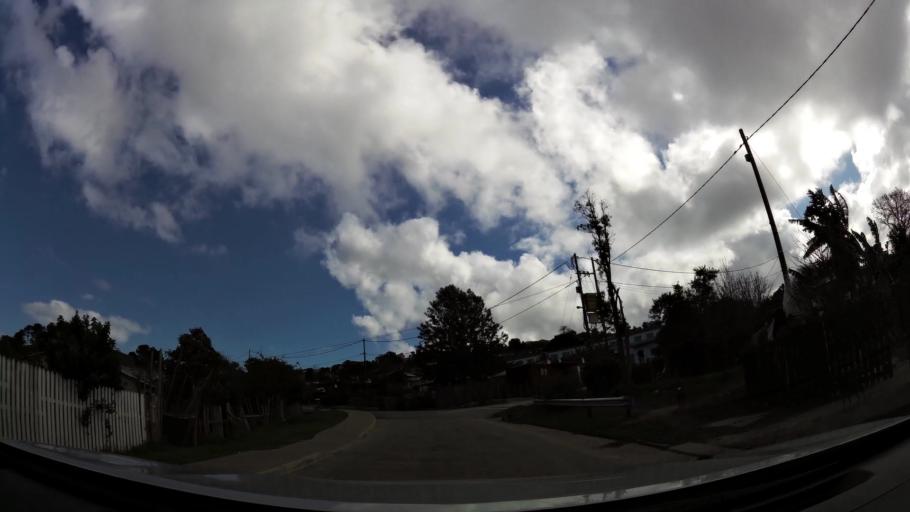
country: ZA
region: Western Cape
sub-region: Eden District Municipality
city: Knysna
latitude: -34.0499
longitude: 23.0928
